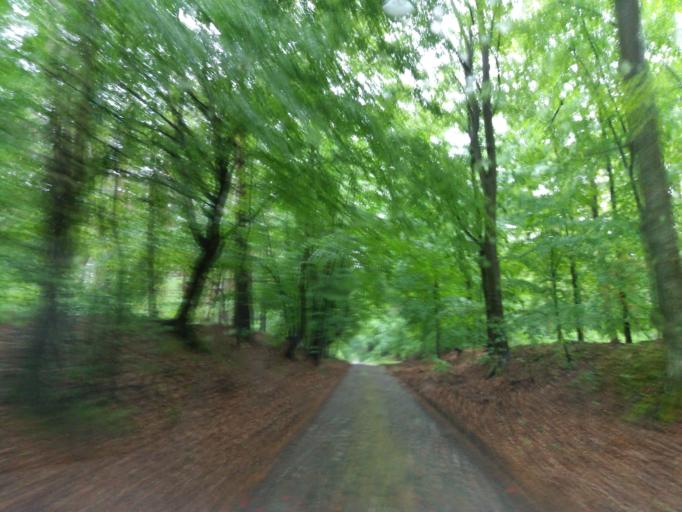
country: PL
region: Lubusz
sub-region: Powiat strzelecko-drezdenecki
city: Dobiegniew
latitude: 53.0287
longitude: 15.9040
